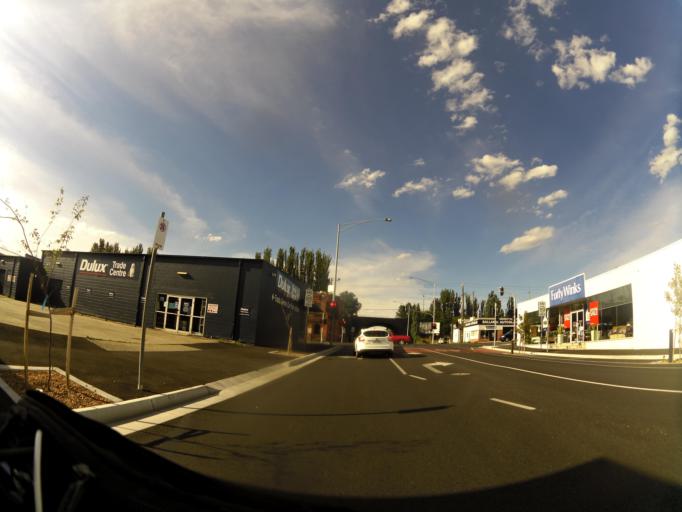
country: AU
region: Victoria
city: Ballarat East
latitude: -37.5610
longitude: 143.8641
